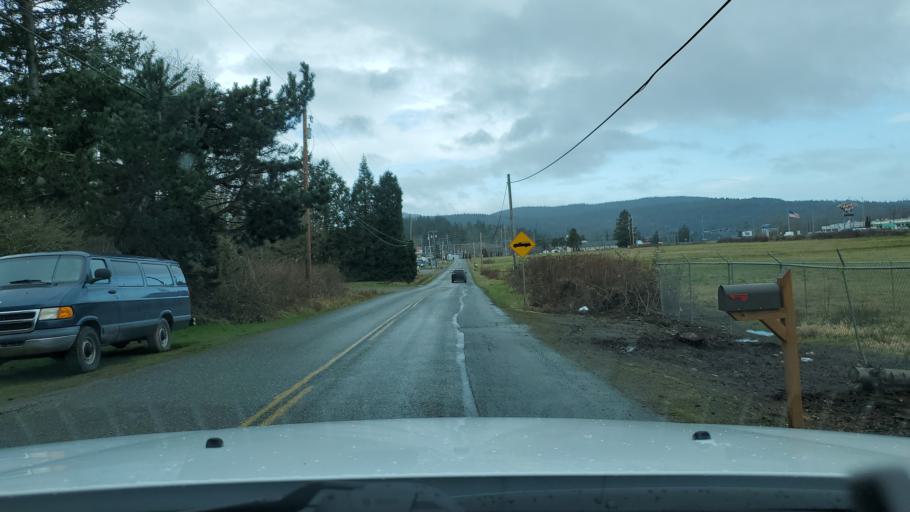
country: US
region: Washington
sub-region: Skagit County
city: Anacortes
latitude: 48.4584
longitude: -122.5544
